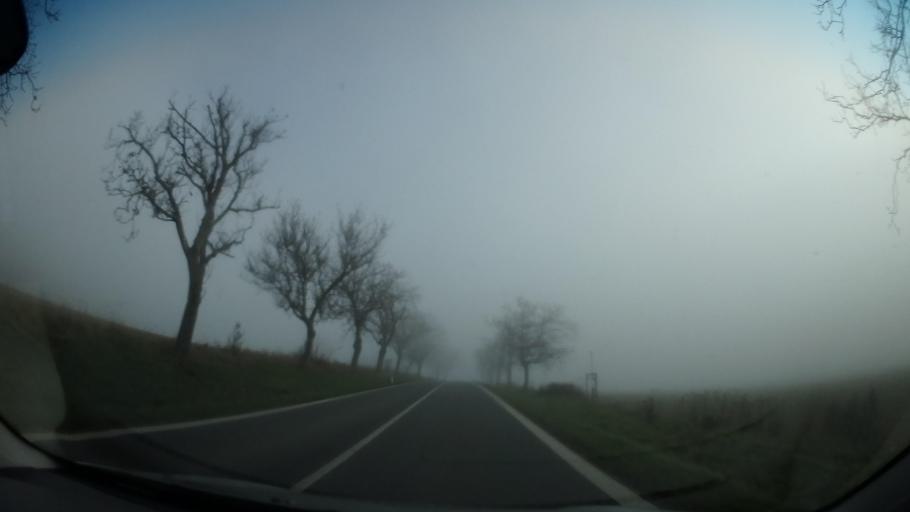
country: CZ
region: South Moravian
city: Zdanice
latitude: 49.0448
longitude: 16.9919
